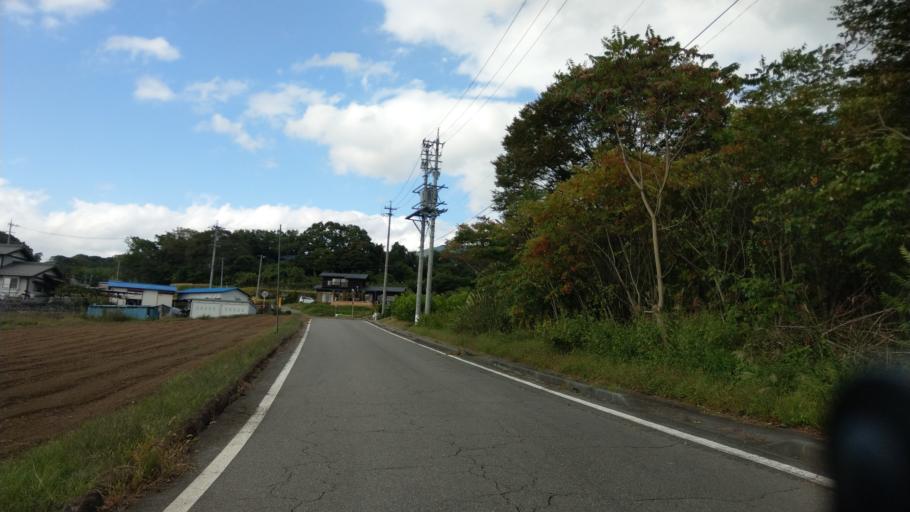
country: JP
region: Nagano
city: Komoro
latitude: 36.3470
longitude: 138.4138
